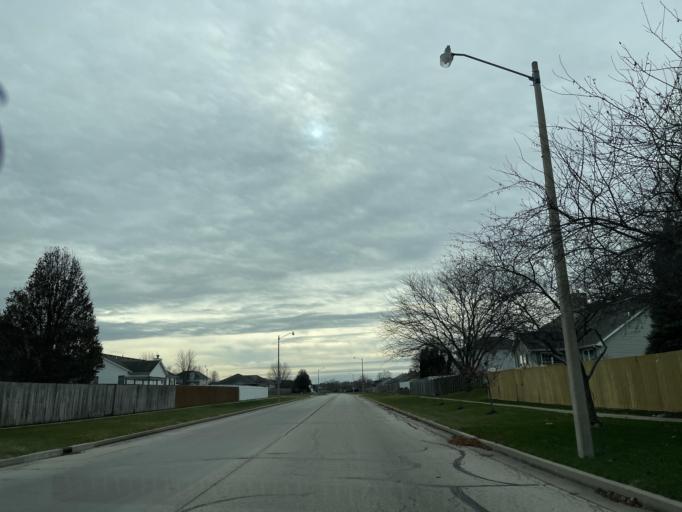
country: US
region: Illinois
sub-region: Sangamon County
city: Jerome
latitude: 39.7655
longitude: -89.7298
